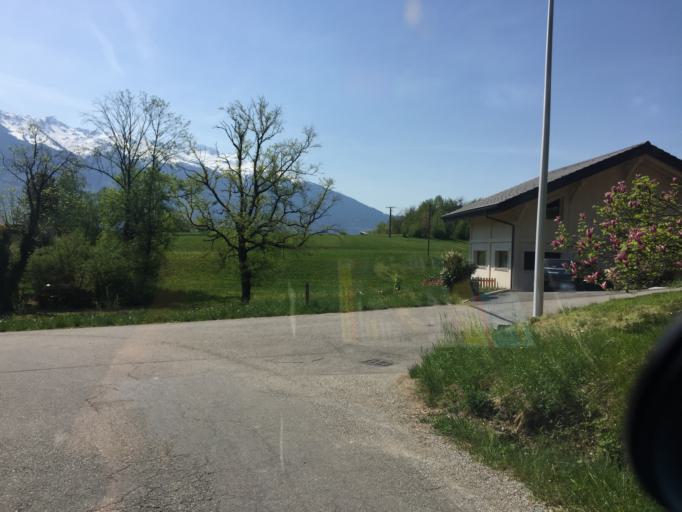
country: FR
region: Rhone-Alpes
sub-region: Departement de la Savoie
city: Mercury
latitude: 45.6746
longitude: 6.3417
